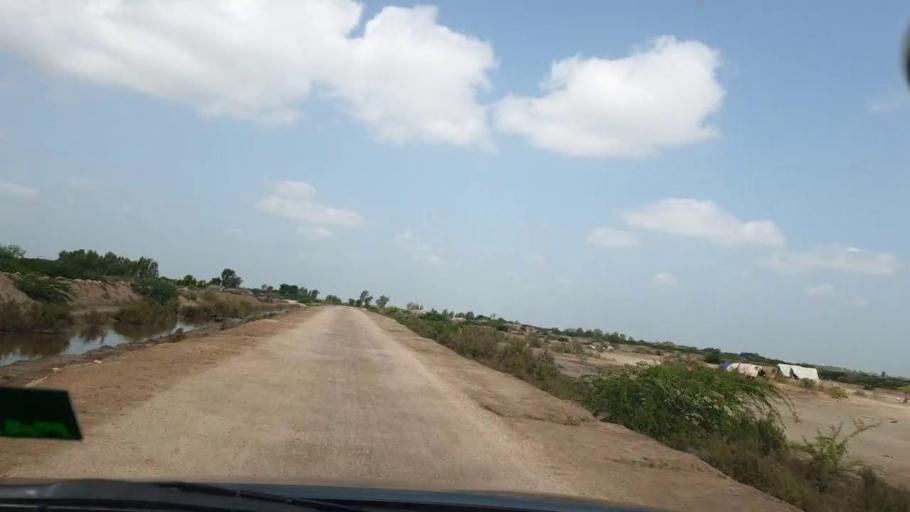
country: PK
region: Sindh
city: Kadhan
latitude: 24.6026
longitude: 69.1215
